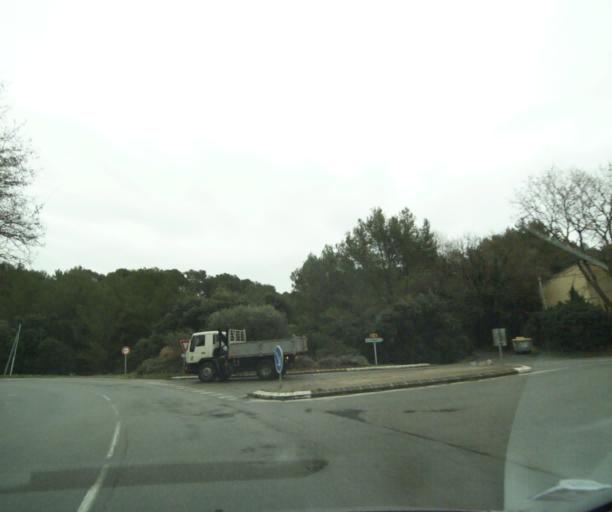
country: FR
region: Provence-Alpes-Cote d'Azur
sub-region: Departement des Bouches-du-Rhone
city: Rognes
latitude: 43.6629
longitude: 5.3388
